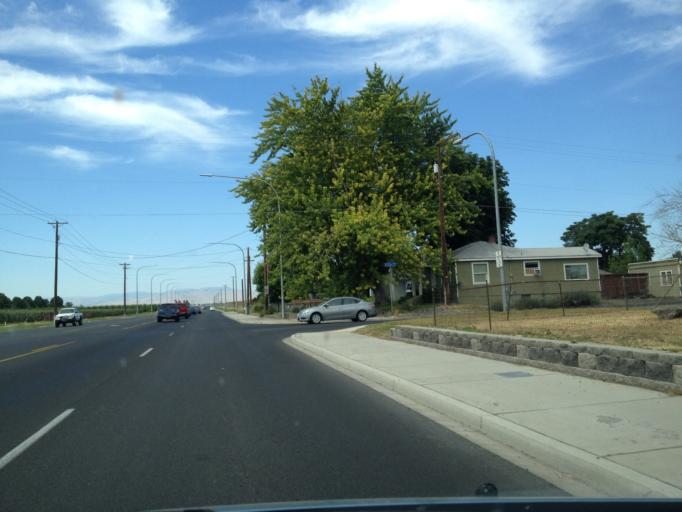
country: US
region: Washington
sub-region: Yakima County
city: West Valley
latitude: 46.5855
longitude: -120.5783
